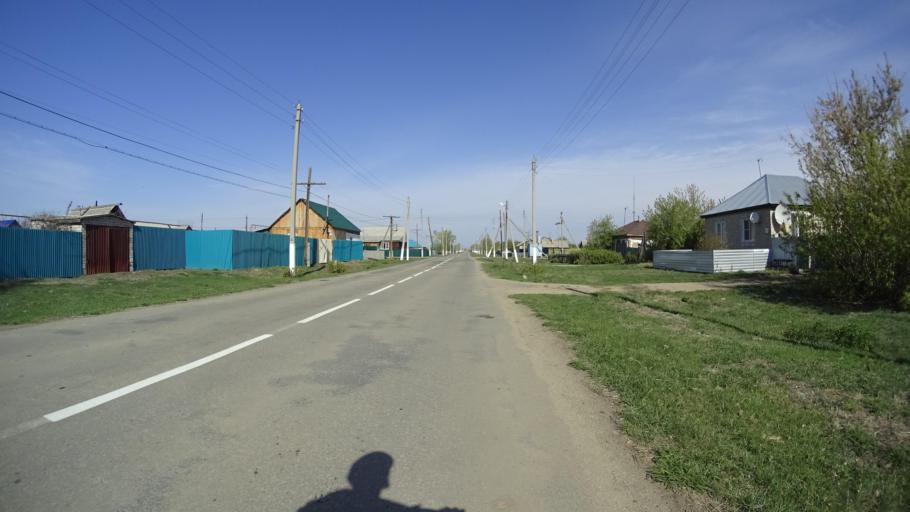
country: RU
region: Chelyabinsk
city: Chesma
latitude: 53.7985
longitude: 61.0265
